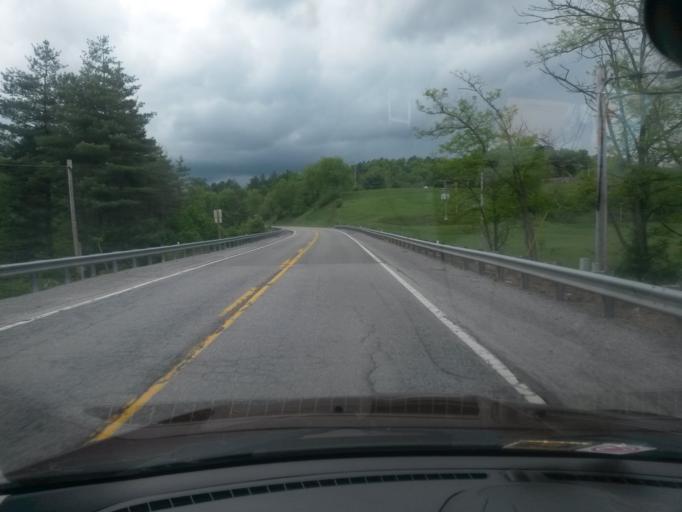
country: US
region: Virginia
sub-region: Floyd County
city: Floyd
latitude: 36.9386
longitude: -80.3408
